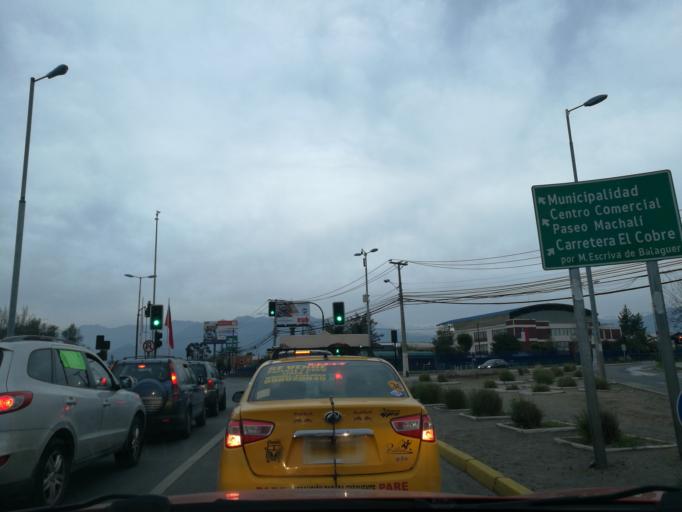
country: CL
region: O'Higgins
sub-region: Provincia de Cachapoal
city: Machali
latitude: -34.1765
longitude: -70.6961
